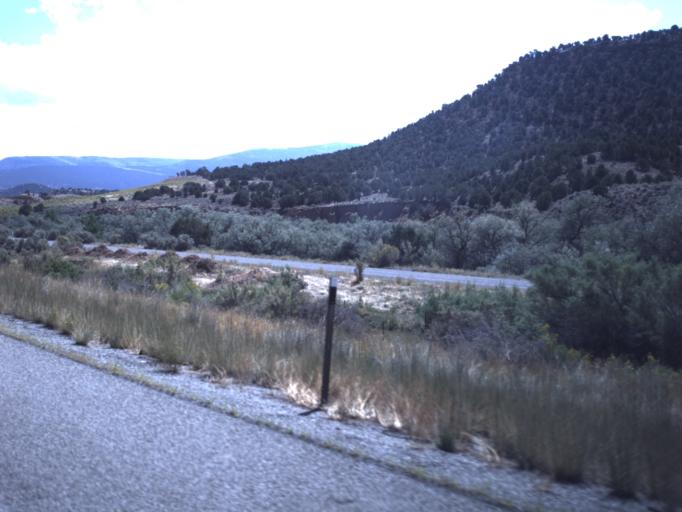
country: US
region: Utah
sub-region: Sevier County
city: Salina
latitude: 38.9210
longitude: -111.7600
